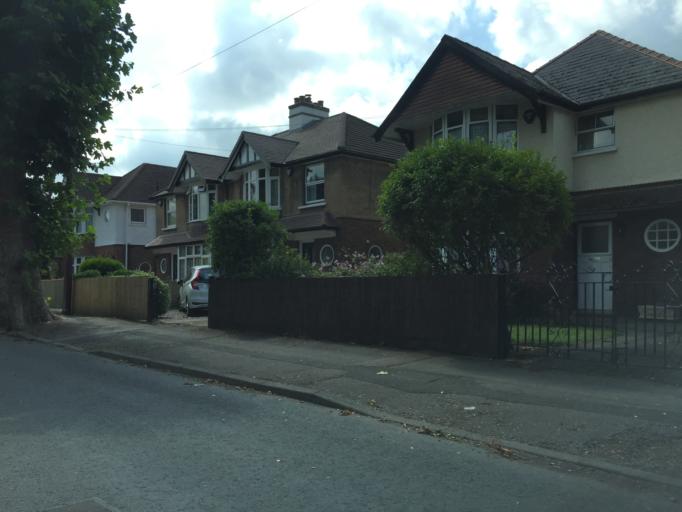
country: GB
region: England
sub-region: Gloucestershire
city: Gloucester
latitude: 51.8724
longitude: -2.2370
